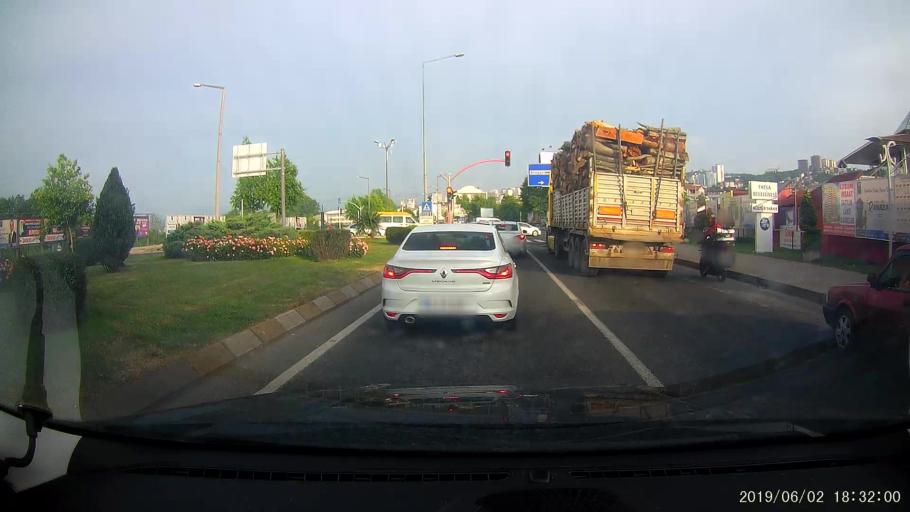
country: TR
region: Ordu
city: Fatsa
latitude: 41.0359
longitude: 37.4939
